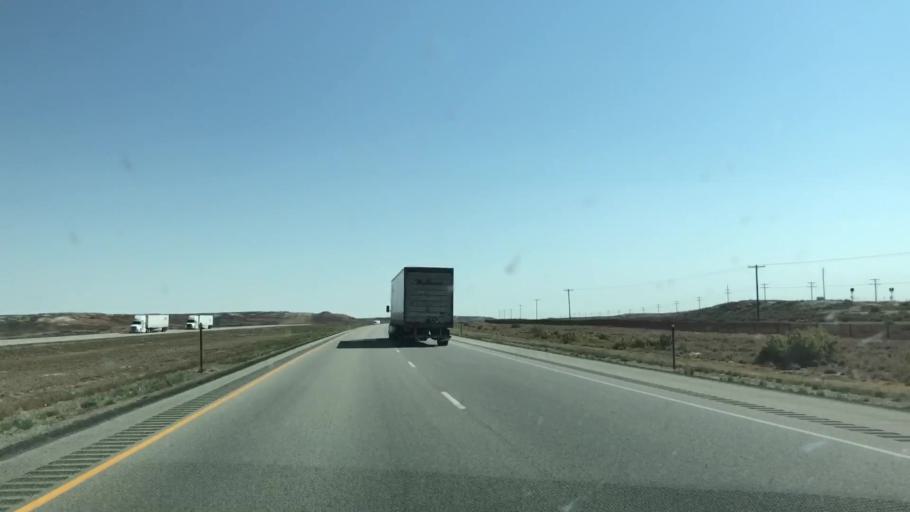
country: US
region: Wyoming
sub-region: Carbon County
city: Rawlins
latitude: 41.7041
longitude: -107.8951
